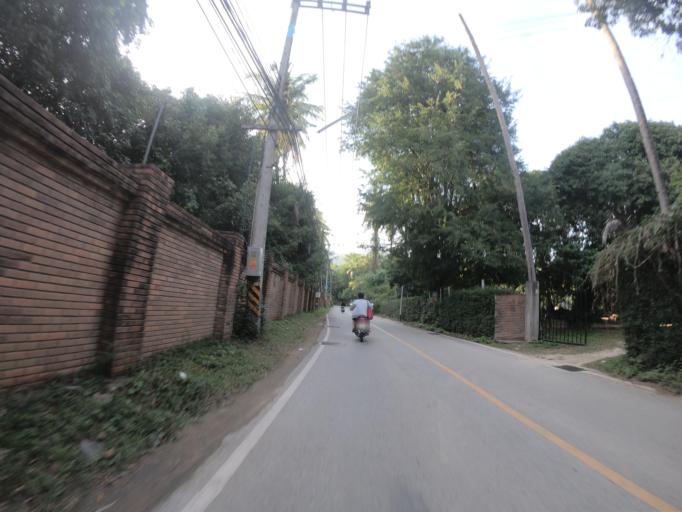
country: TH
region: Chiang Mai
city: Chiang Mai
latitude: 18.8184
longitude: 98.9531
